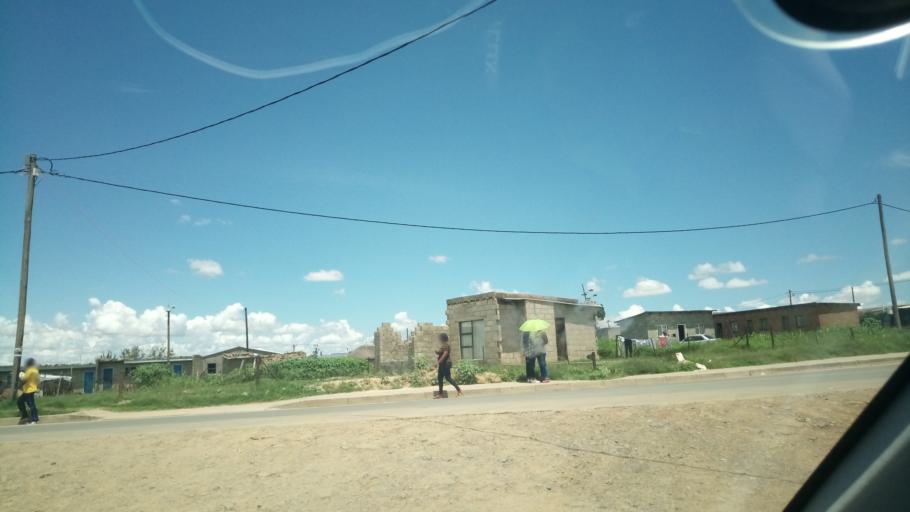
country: LS
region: Maseru
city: Maseru
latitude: -29.3660
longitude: 27.5413
